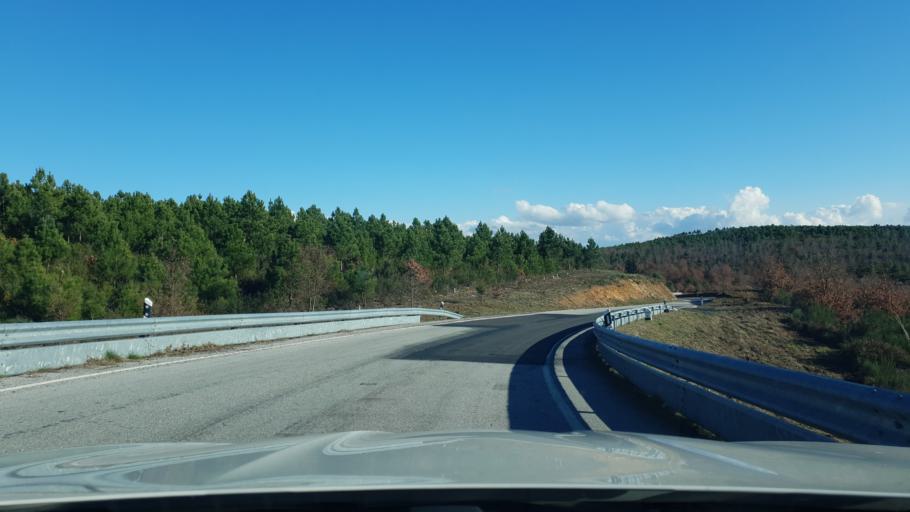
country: PT
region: Braganca
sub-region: Freixo de Espada A Cinta
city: Freixo de Espada a Cinta
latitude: 41.1400
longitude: -6.8075
